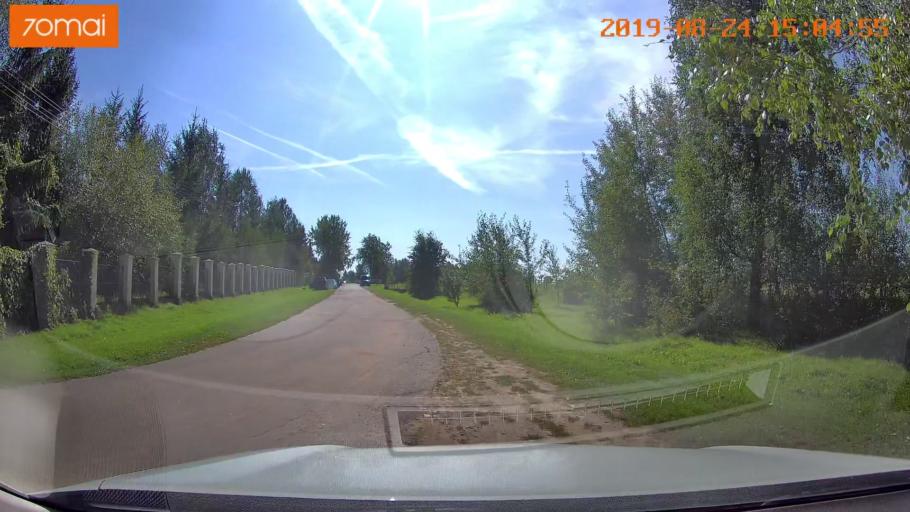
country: BY
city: Michanovichi
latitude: 53.5974
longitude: 27.6842
